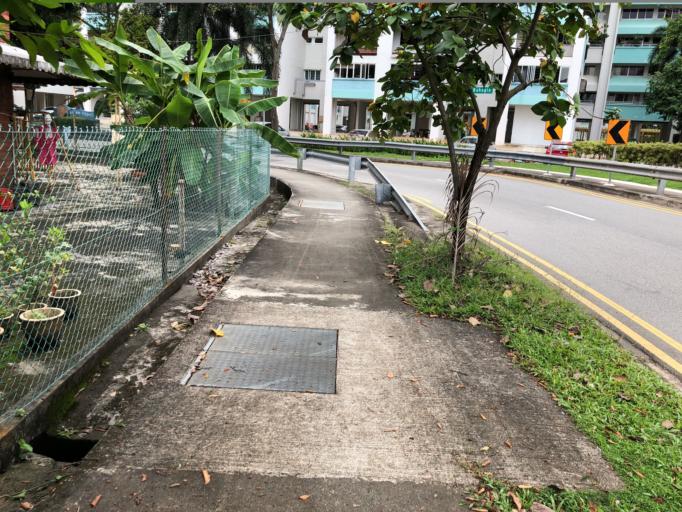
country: SG
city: Singapore
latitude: 1.3279
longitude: 103.8560
